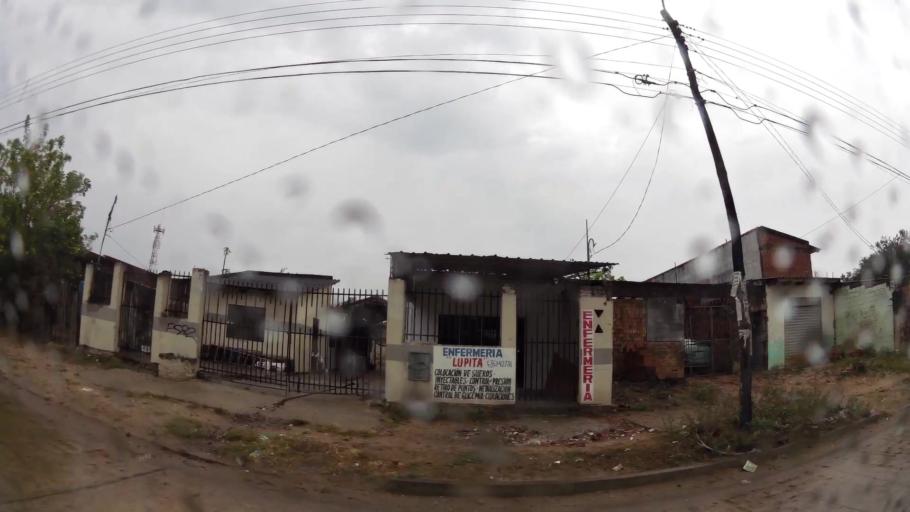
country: BO
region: Santa Cruz
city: Santa Cruz de la Sierra
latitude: -17.8063
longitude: -63.1358
